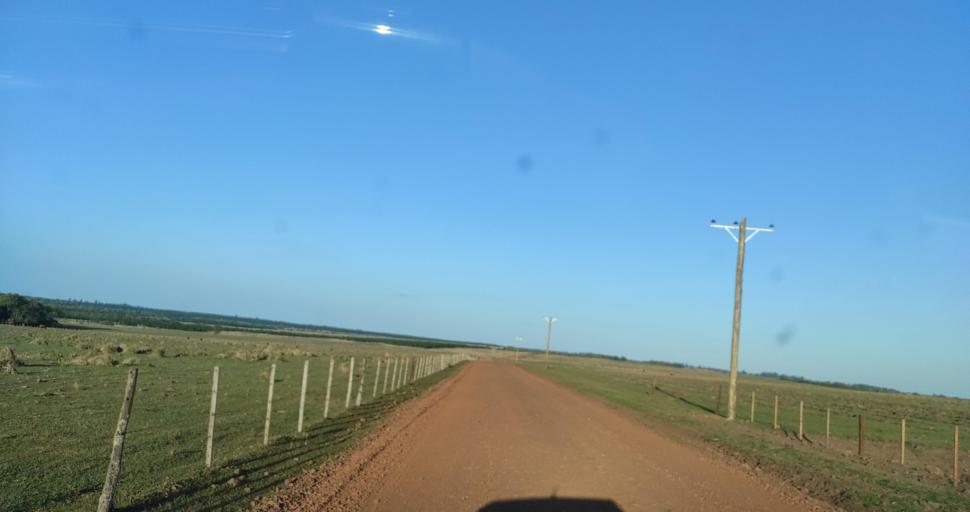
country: PY
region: Itapua
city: Carmen del Parana
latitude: -27.4108
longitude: -56.1505
